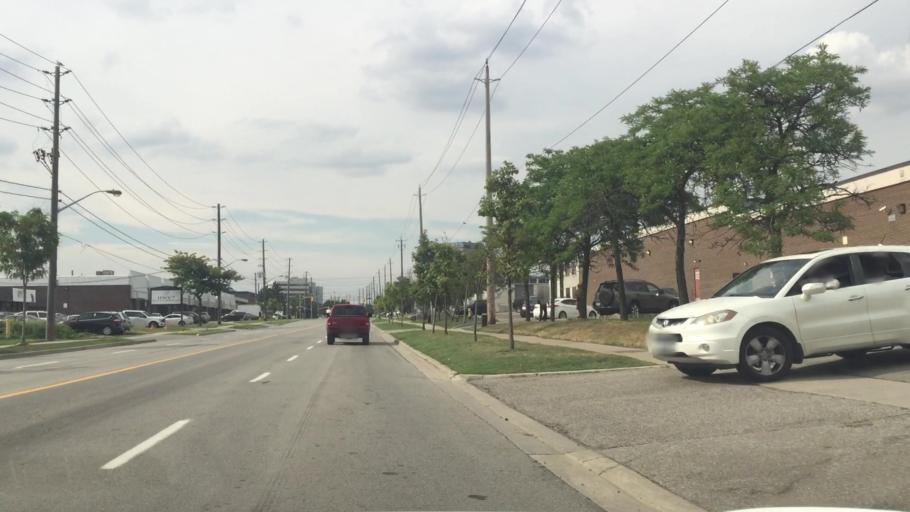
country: CA
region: Ontario
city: Concord
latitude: 43.7662
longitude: -79.5413
